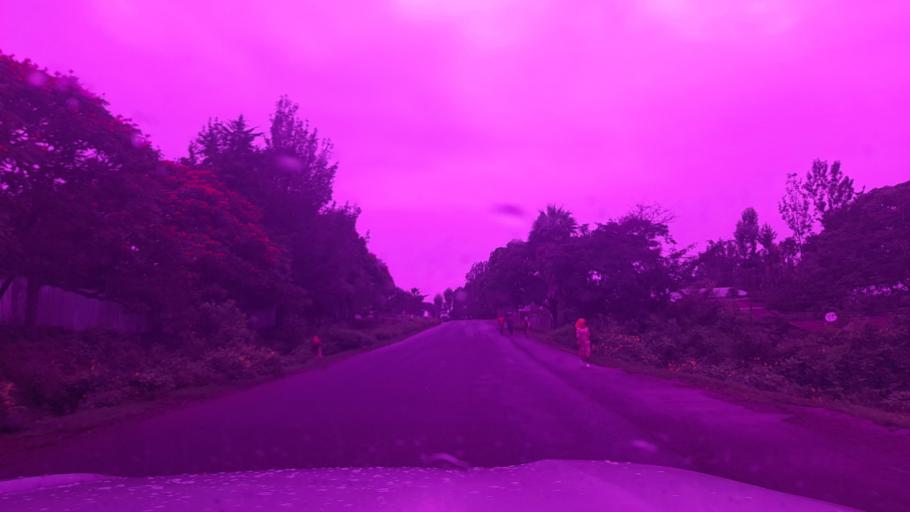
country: ET
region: Oromiya
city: Jima
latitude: 7.8394
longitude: 37.3639
